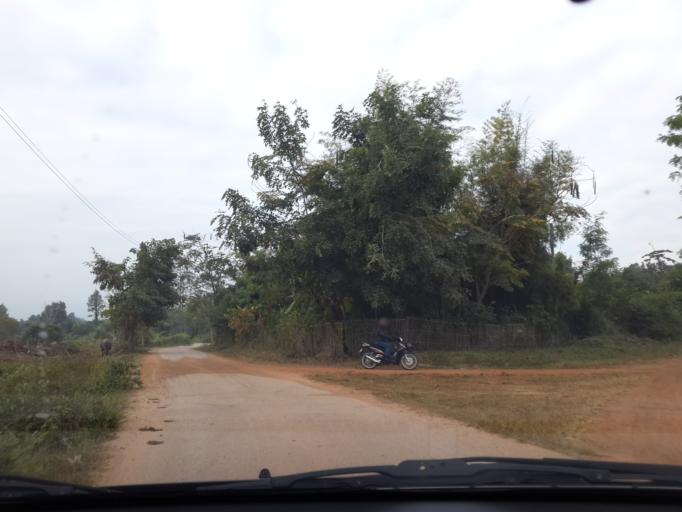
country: TH
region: Chiang Mai
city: San Sai
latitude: 18.9115
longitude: 99.1107
